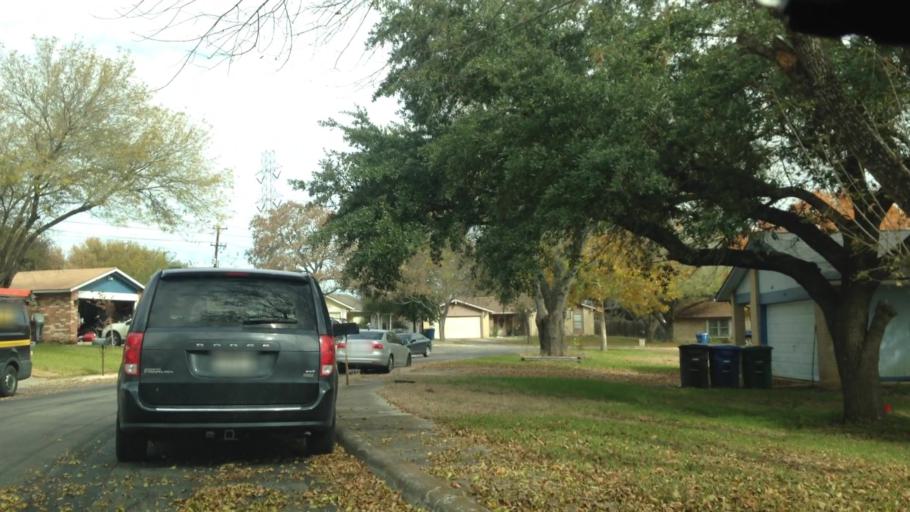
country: US
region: Texas
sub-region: Bexar County
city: Windcrest
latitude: 29.5796
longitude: -98.4063
